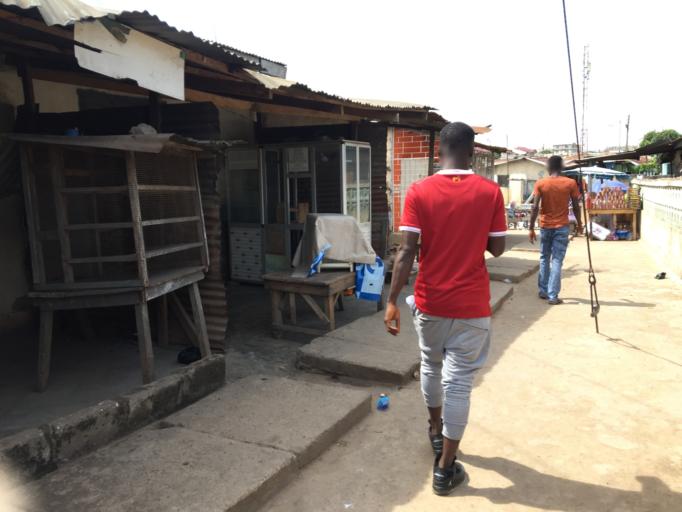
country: GH
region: Greater Accra
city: Accra
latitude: 5.5880
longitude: -0.1947
